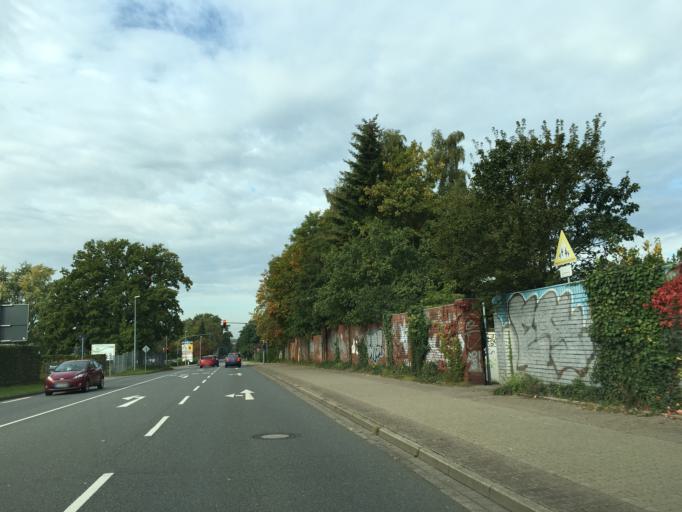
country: DE
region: Lower Saxony
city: Adendorf
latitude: 53.2609
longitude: 10.4403
